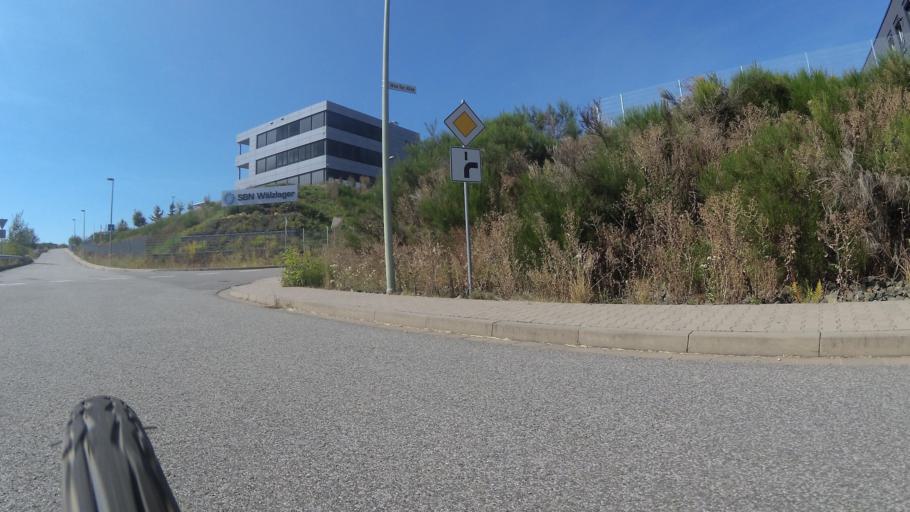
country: DE
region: Rheinland-Pfalz
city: Schonenberg-Kubelberg
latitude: 49.4036
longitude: 7.3467
